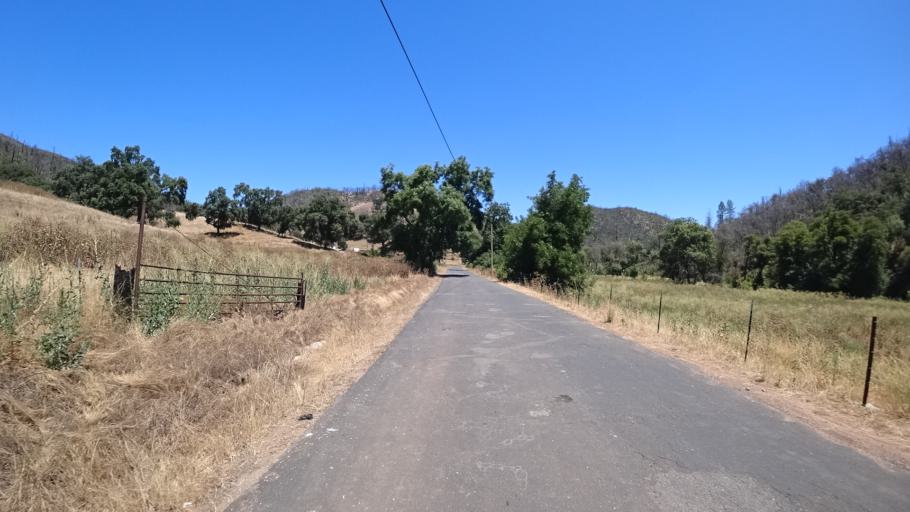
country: US
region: California
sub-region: Calaveras County
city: San Andreas
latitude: 38.2850
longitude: -120.6480
